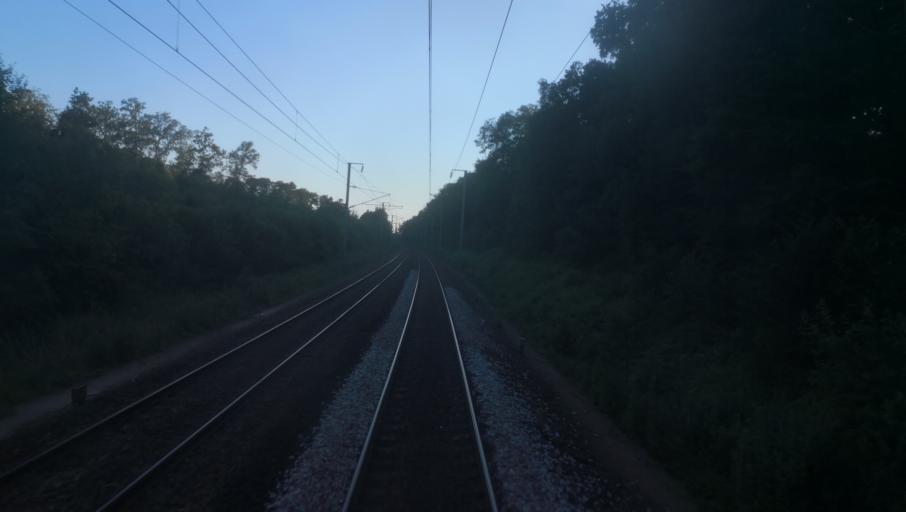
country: FR
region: Haute-Normandie
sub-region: Departement de l'Eure
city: Bernay
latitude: 49.0910
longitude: 0.5287
